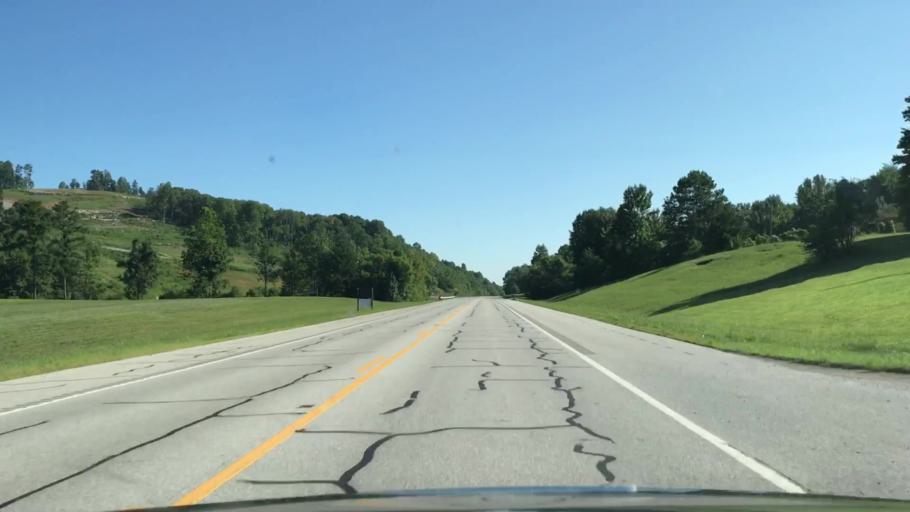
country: US
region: Tennessee
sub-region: Clay County
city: Celina
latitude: 36.6094
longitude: -85.4244
